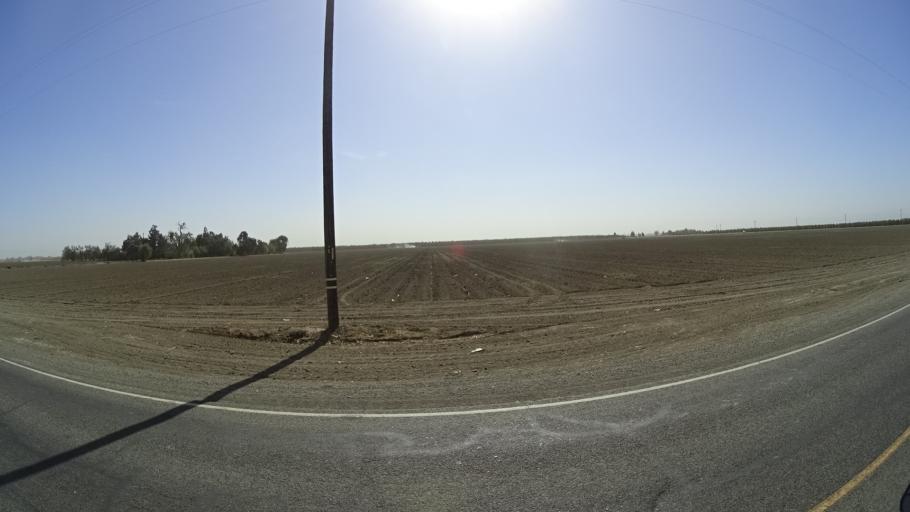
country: US
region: California
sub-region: Yolo County
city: Davis
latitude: 38.5905
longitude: -121.7986
